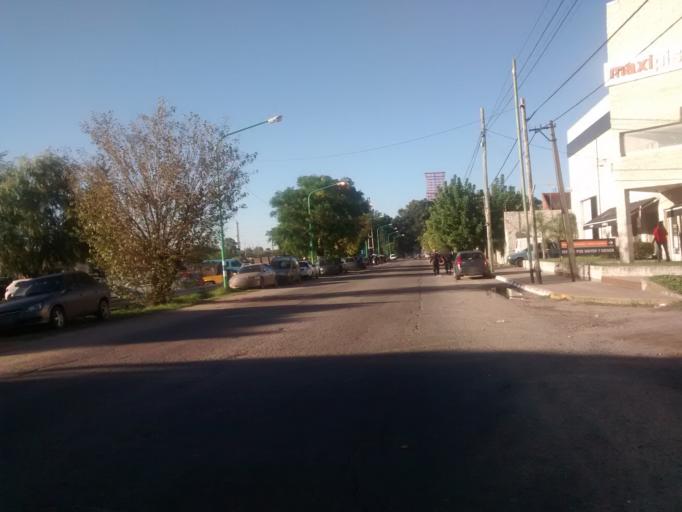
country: AR
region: Buenos Aires
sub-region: Partido de La Plata
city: La Plata
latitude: -34.8976
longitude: -57.9311
